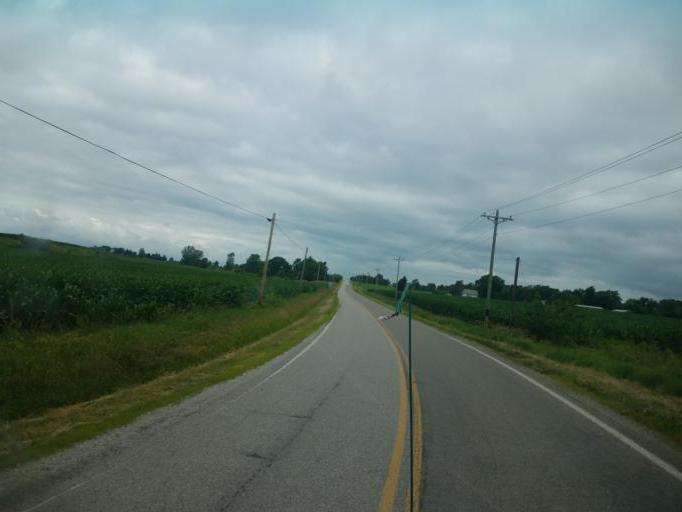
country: US
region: Ohio
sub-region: Union County
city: Richwood
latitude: 40.4148
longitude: -83.4687
